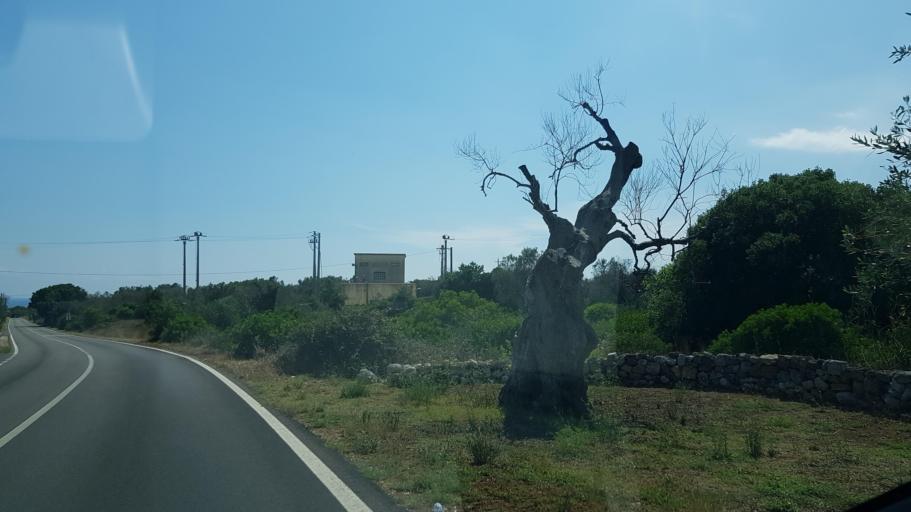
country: IT
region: Apulia
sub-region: Provincia di Lecce
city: Leuca
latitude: 39.8121
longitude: 18.3546
